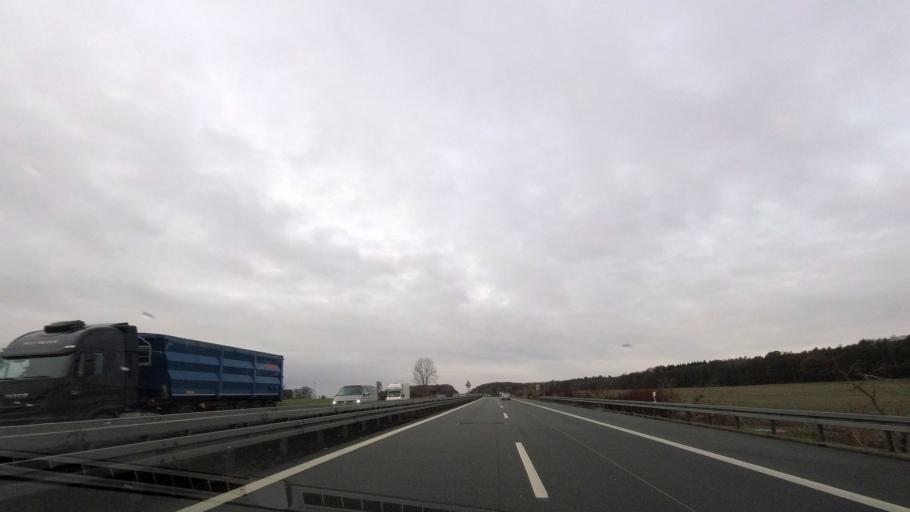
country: DE
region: Brandenburg
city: Gerdshagen
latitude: 53.2511
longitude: 12.1725
